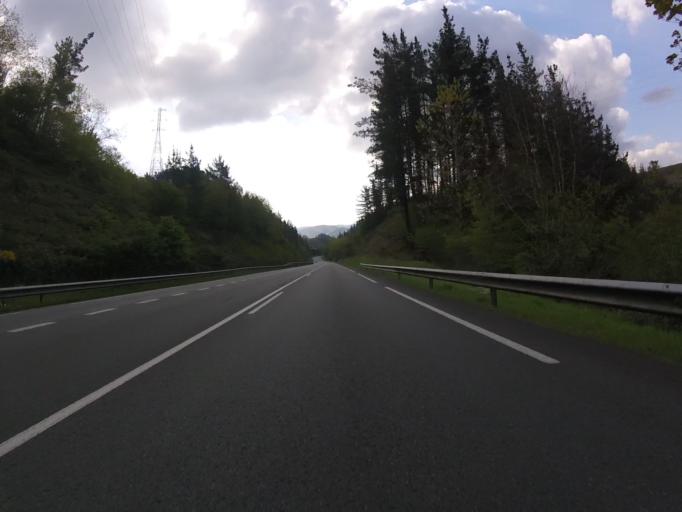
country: ES
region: Basque Country
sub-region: Provincia de Guipuzcoa
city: Azkoitia
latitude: 43.1916
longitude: -2.3329
